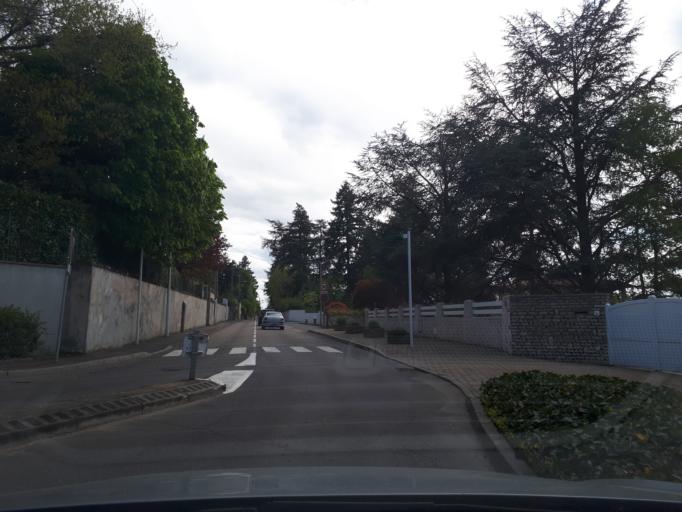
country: FR
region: Rhone-Alpes
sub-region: Departement de la Loire
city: Saint-Galmier
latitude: 45.6030
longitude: 4.3138
